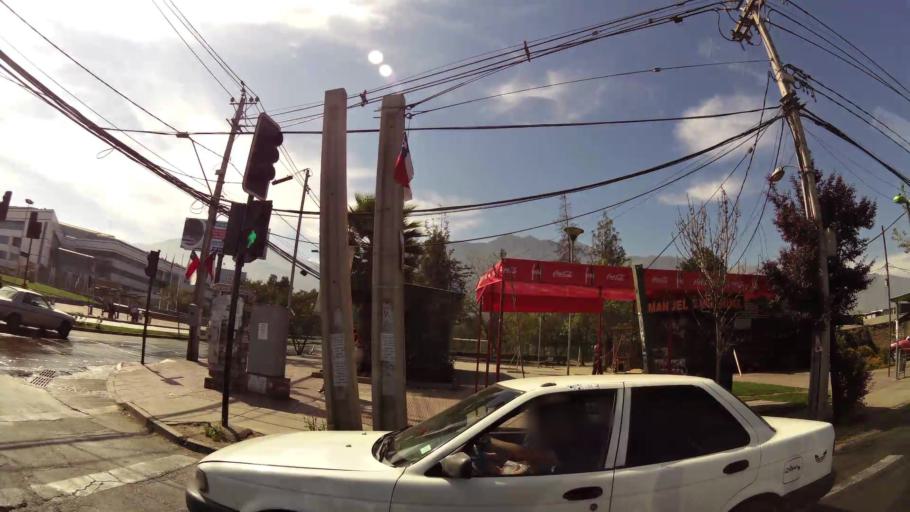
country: CL
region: Santiago Metropolitan
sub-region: Provincia de Santiago
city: Villa Presidente Frei, Nunoa, Santiago, Chile
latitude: -33.4517
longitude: -70.5400
